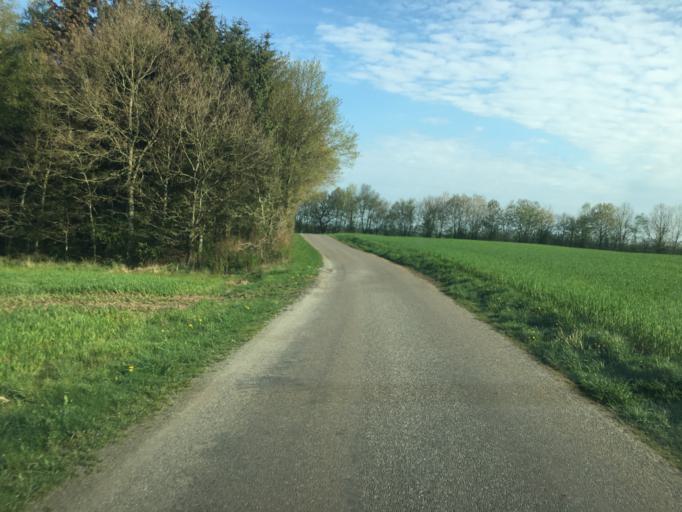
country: DK
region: South Denmark
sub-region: Aabenraa Kommune
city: Rodekro
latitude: 55.1363
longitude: 9.3804
